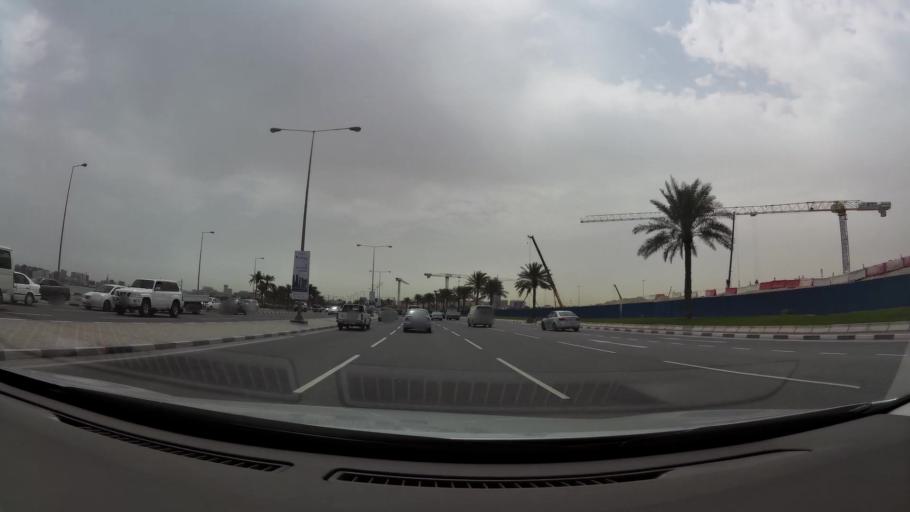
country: QA
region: Baladiyat ad Dawhah
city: Doha
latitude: 25.3033
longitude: 51.5175
